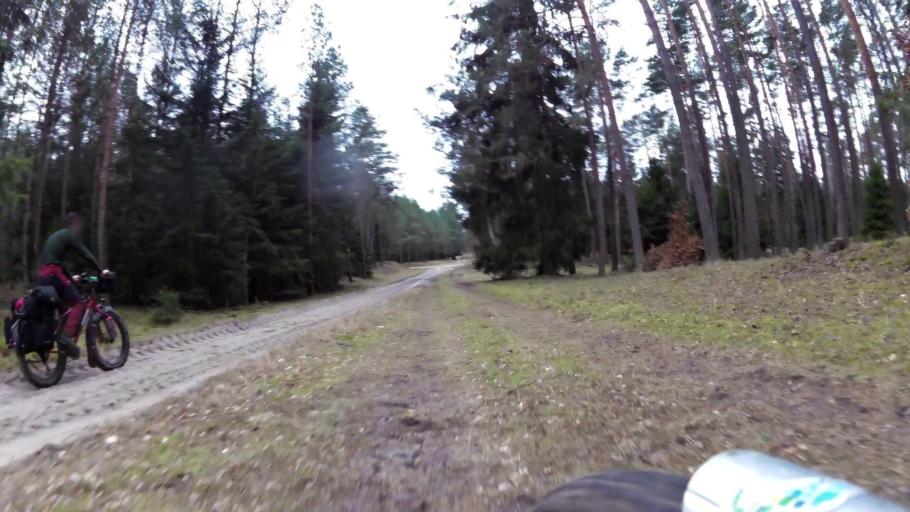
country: PL
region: Pomeranian Voivodeship
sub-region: Powiat bytowski
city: Trzebielino
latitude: 54.1235
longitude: 17.1310
